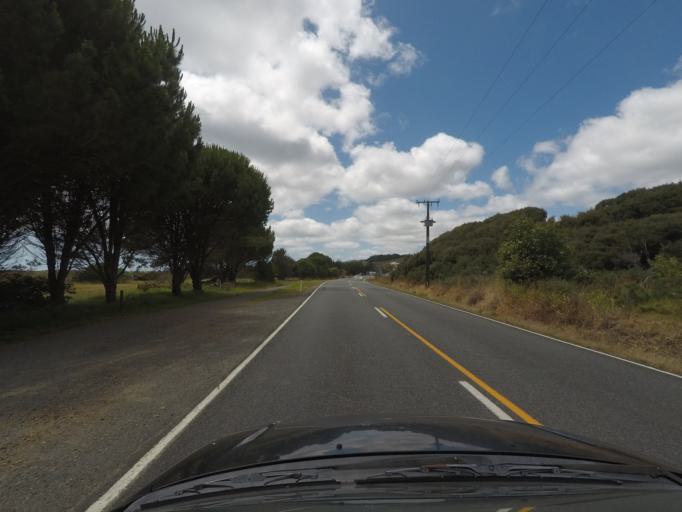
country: NZ
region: Northland
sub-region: Whangarei
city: Ruakaka
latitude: -36.0242
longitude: 174.4992
